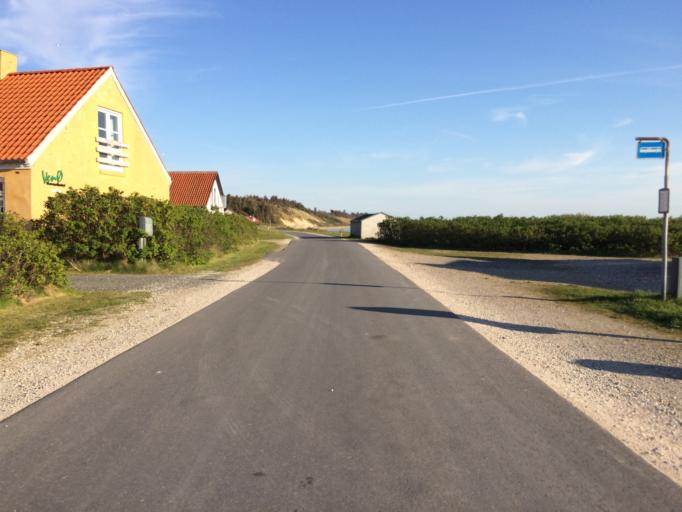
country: DK
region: Central Jutland
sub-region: Struer Kommune
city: Struer
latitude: 56.5507
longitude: 8.6165
